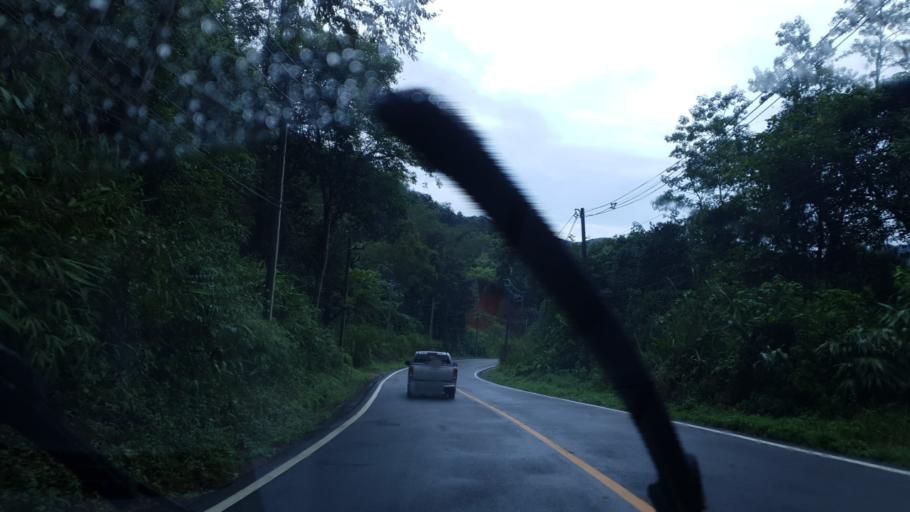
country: TH
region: Mae Hong Son
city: Ban Huai I Huak
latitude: 18.1423
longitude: 98.0923
